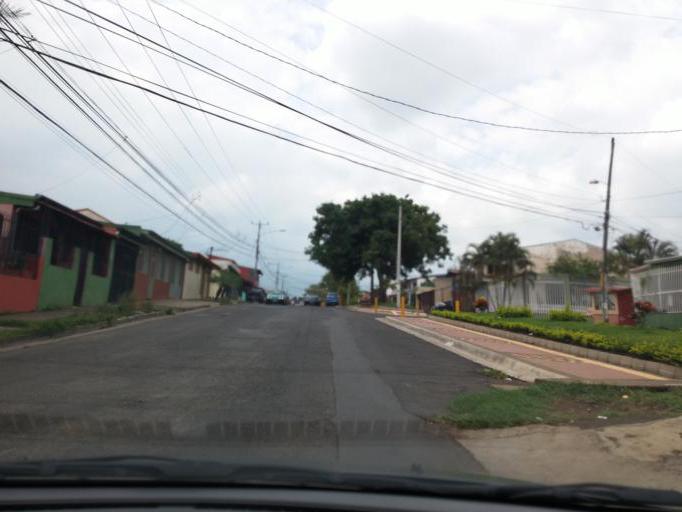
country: CR
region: Alajuela
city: Alajuela
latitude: 10.0077
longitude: -84.2042
